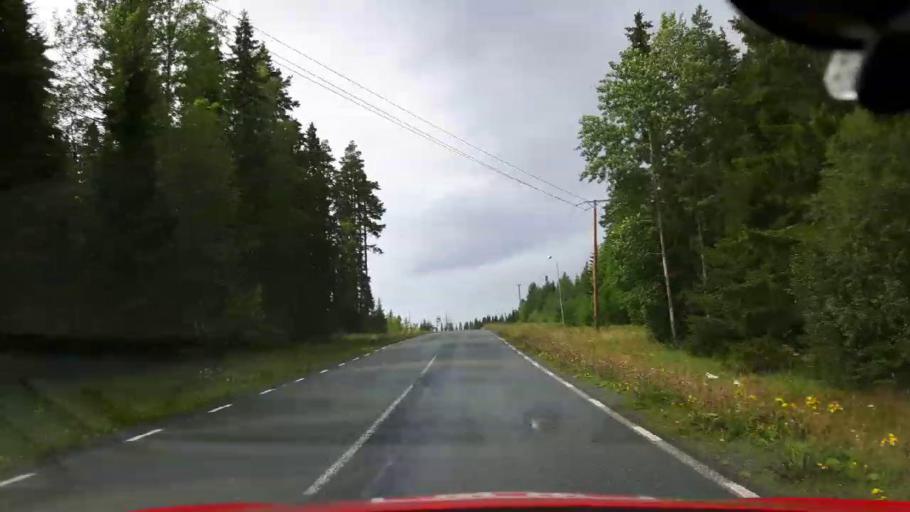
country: SE
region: Jaemtland
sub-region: Krokoms Kommun
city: Krokom
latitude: 63.3494
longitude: 14.2342
